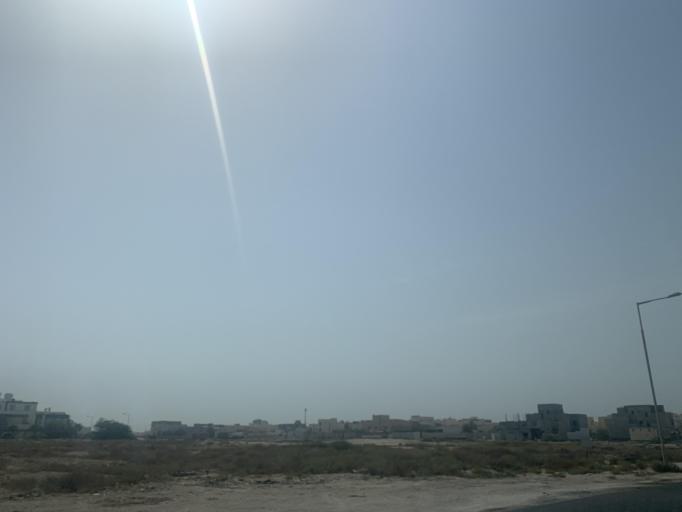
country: BH
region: Manama
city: Jidd Hafs
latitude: 26.2050
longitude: 50.4648
